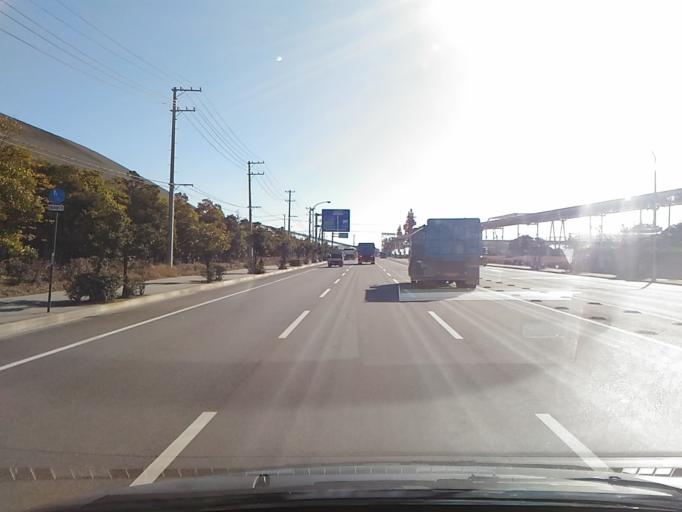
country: JP
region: Fukushima
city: Iwaki
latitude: 36.9383
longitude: 140.8790
